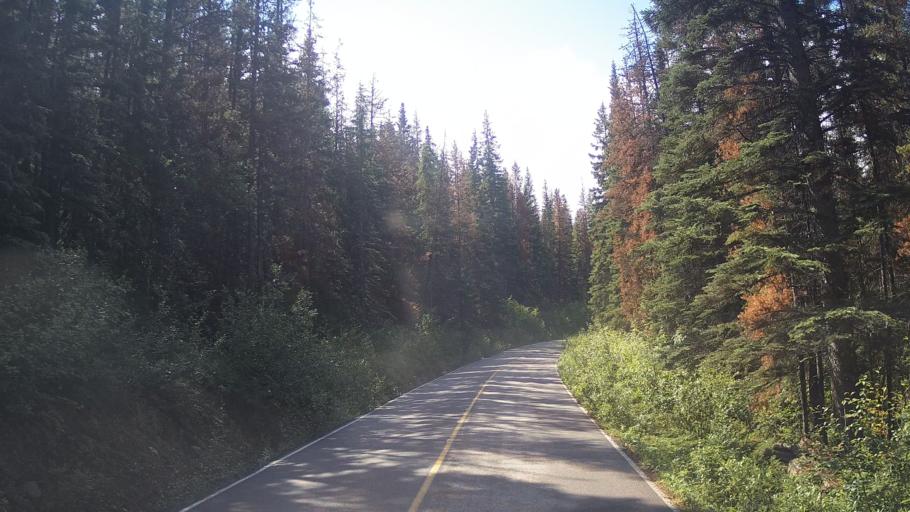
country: CA
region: Alberta
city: Jasper Park Lodge
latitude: 52.7663
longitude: -118.0372
